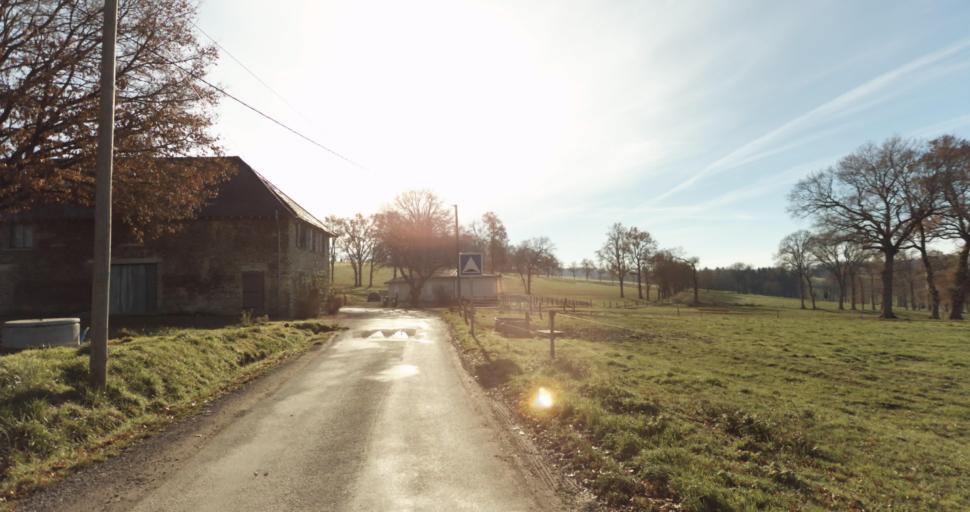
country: FR
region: Limousin
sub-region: Departement de la Haute-Vienne
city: Aixe-sur-Vienne
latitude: 45.7830
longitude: 1.1163
